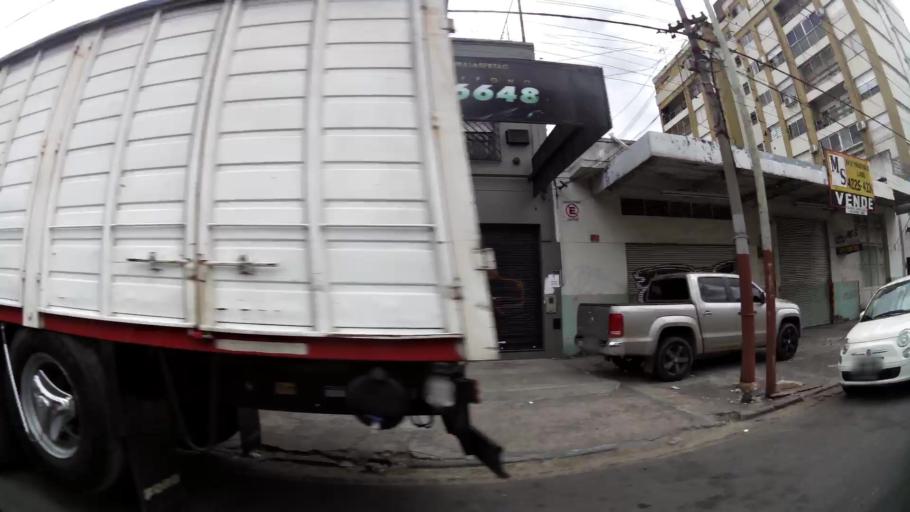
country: AR
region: Buenos Aires
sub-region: Partido de Lanus
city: Lanus
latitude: -34.6971
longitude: -58.3935
